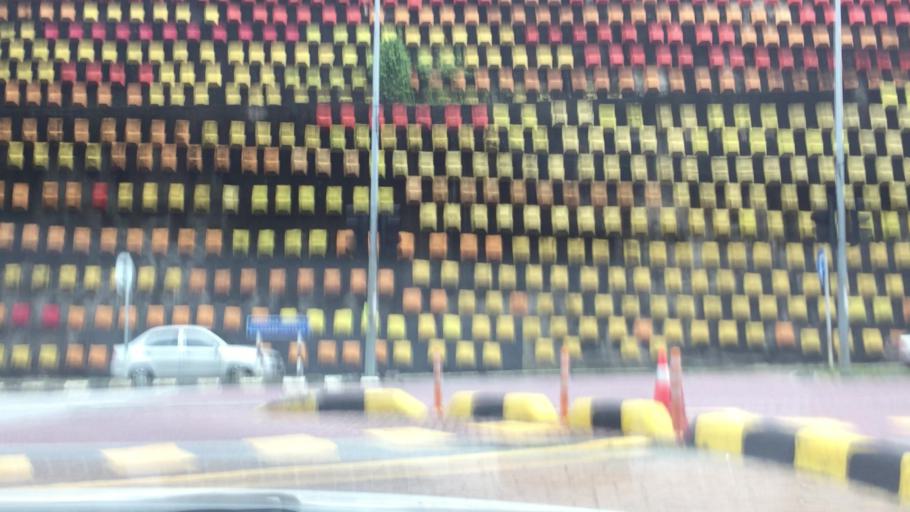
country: MY
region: Kuala Lumpur
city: Kuala Lumpur
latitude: 3.1713
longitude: 101.6638
